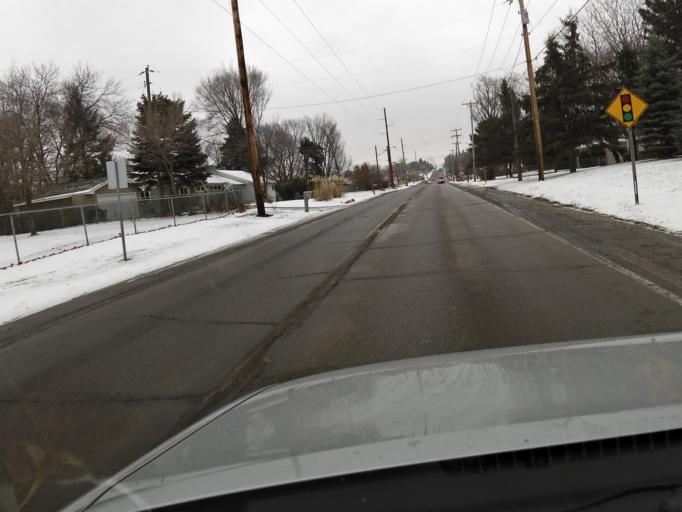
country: US
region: Minnesota
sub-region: Ramsey County
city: Maplewood
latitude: 44.9631
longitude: -92.9878
